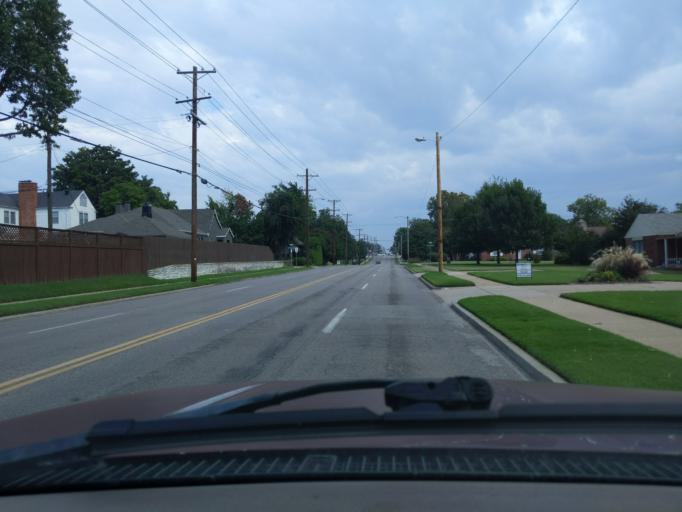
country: US
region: Oklahoma
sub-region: Tulsa County
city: Tulsa
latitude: 36.1332
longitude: -95.9457
